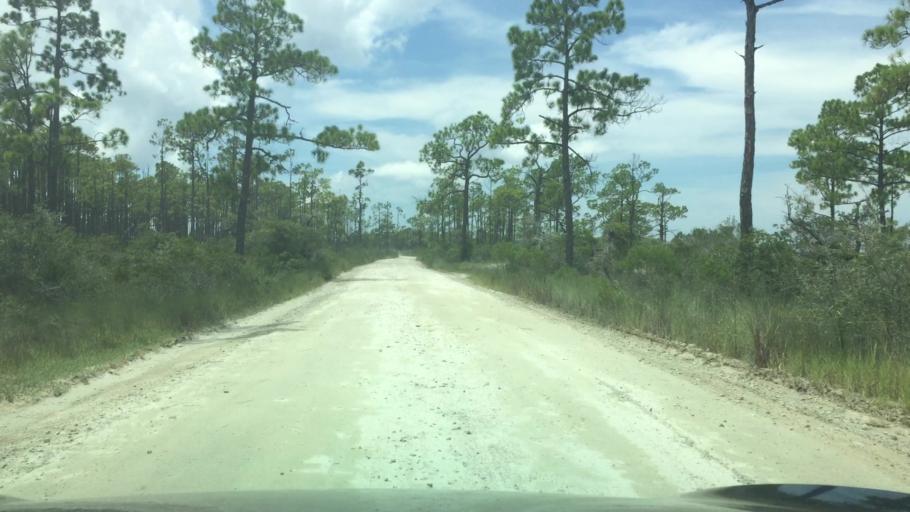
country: US
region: Florida
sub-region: Bay County
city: Mexico Beach
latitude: 29.9621
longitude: -85.4509
